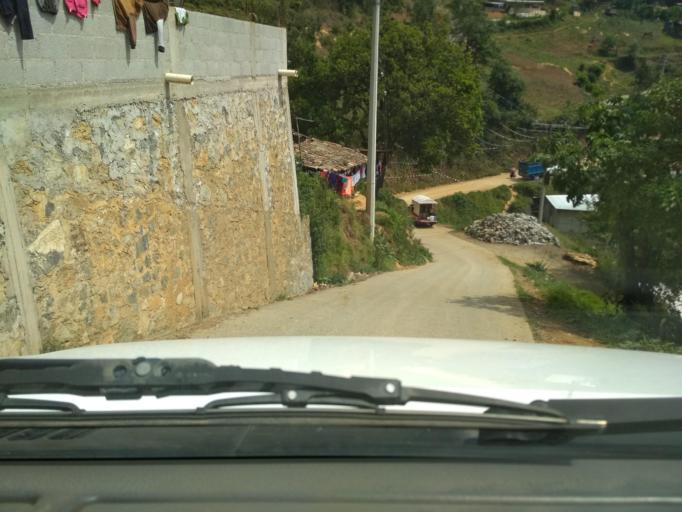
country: MX
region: Veracruz
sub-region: Camerino Z. Mendoza
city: Necoxtla
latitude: 18.7769
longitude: -97.1565
